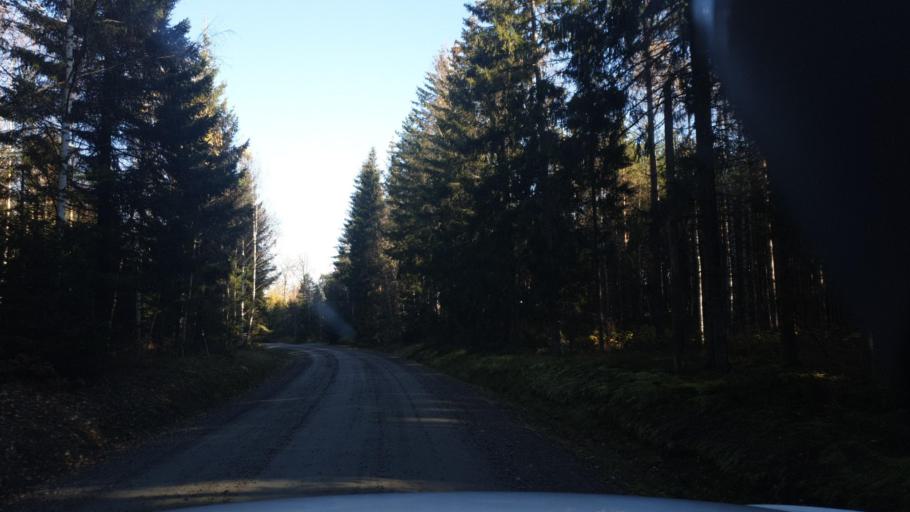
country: SE
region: Vaermland
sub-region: Karlstads Kommun
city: Edsvalla
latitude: 59.5056
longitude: 13.2039
